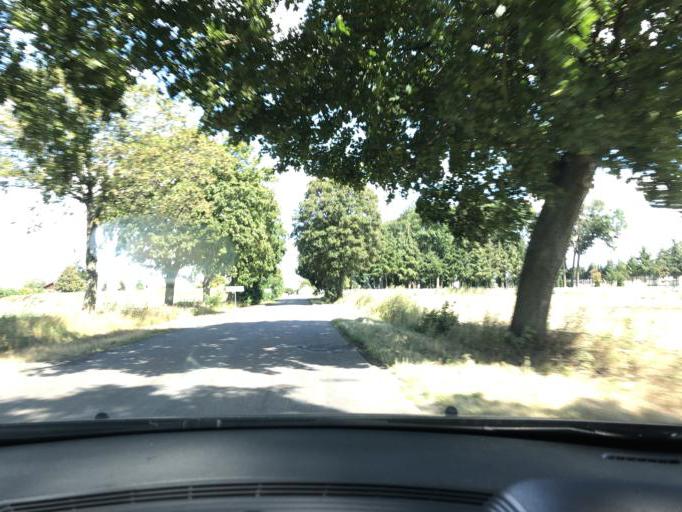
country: PL
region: Lodz Voivodeship
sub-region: Powiat wieruszowski
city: Czastary
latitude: 51.2540
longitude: 18.3170
